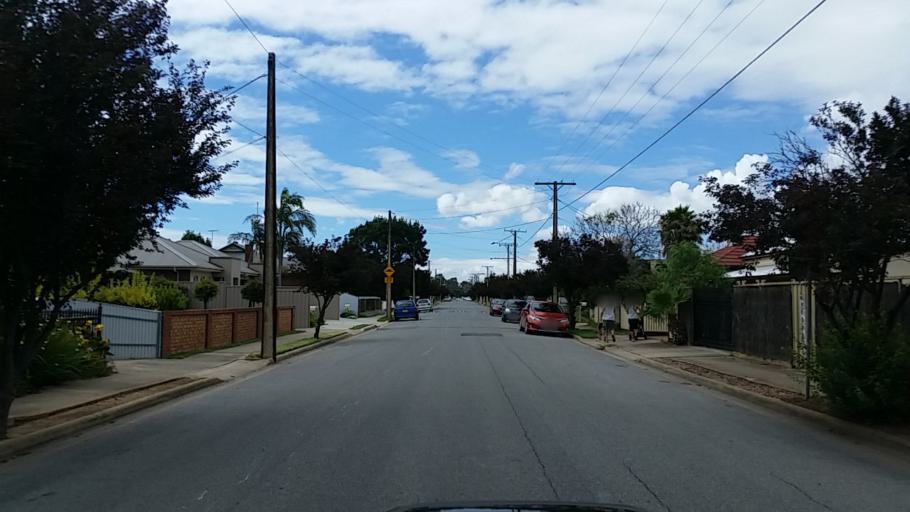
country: AU
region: South Australia
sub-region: Charles Sturt
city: Allenby Gardens
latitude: -34.8964
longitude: 138.5493
